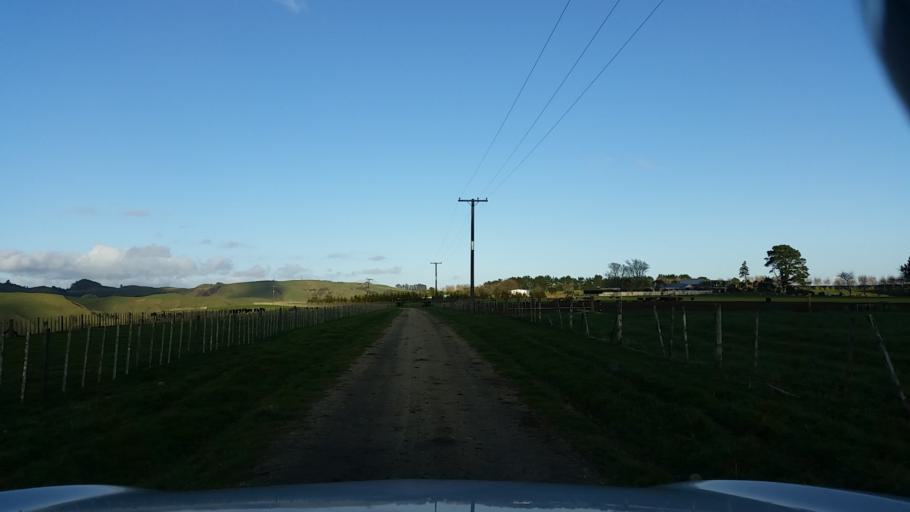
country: NZ
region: Taranaki
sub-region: South Taranaki District
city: Patea
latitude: -39.6153
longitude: 174.4934
